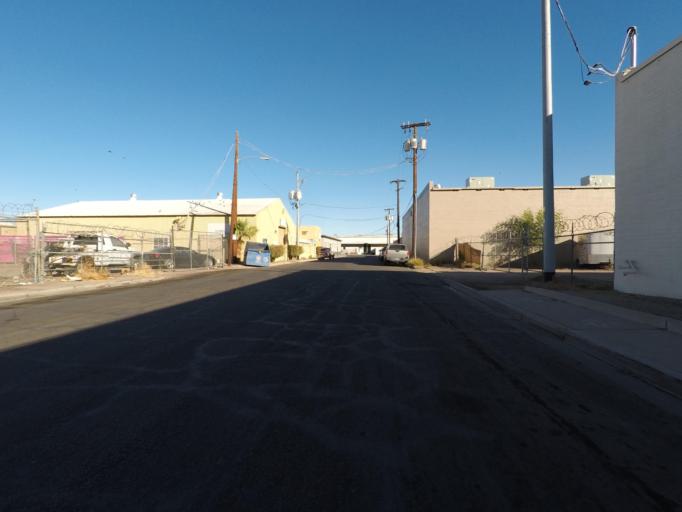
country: US
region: Arizona
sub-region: Maricopa County
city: Phoenix
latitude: 33.4696
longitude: -112.1076
